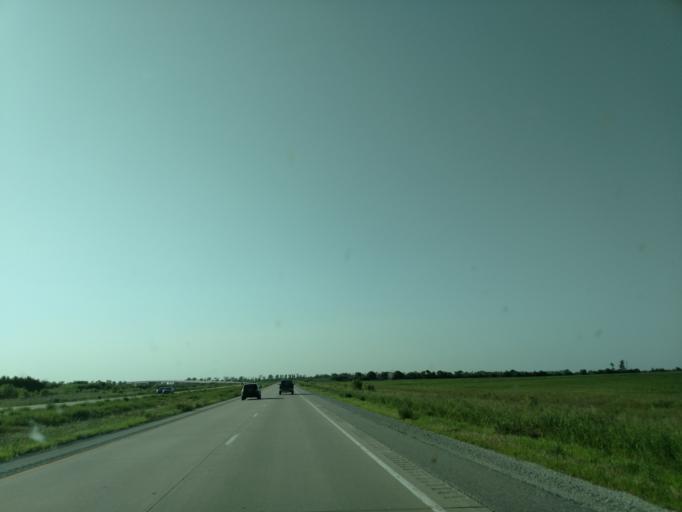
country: US
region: Nebraska
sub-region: Cass County
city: Plattsmouth
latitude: 41.0538
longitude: -95.8648
